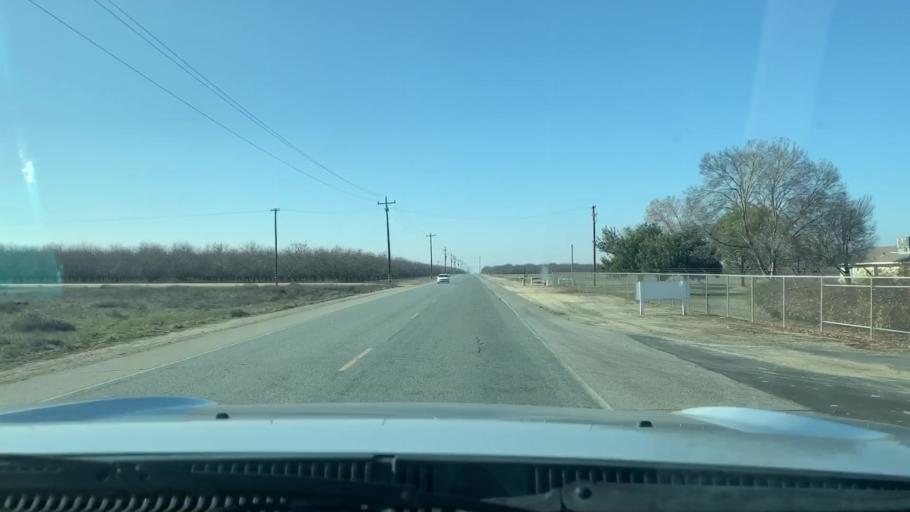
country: US
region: California
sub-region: Kern County
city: Buttonwillow
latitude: 35.5004
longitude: -119.5047
